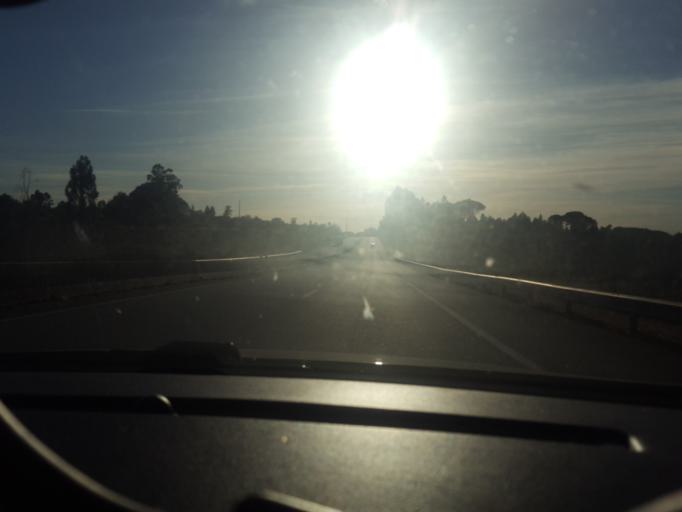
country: PT
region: Viseu
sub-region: Concelho de Carregal do Sal
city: Carregal do Sal
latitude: 40.4625
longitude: -7.9520
